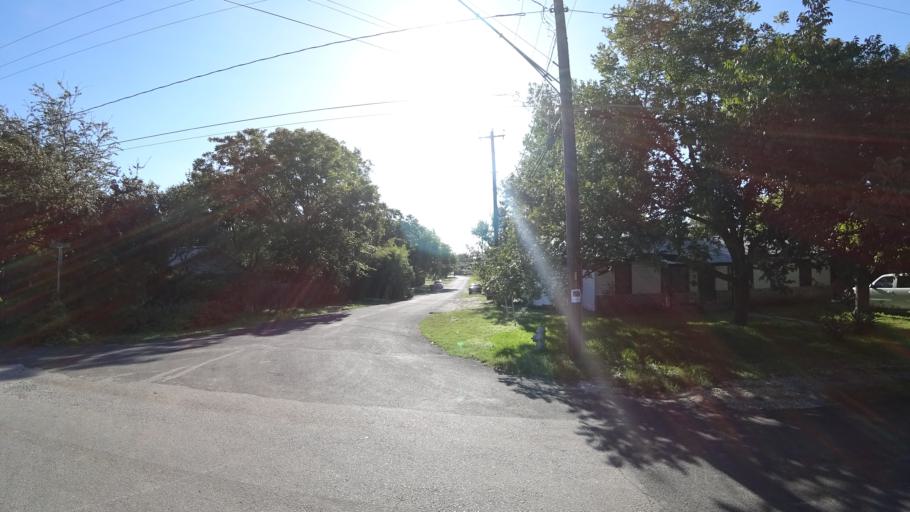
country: US
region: Texas
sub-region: Travis County
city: Wells Branch
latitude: 30.3553
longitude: -97.6949
